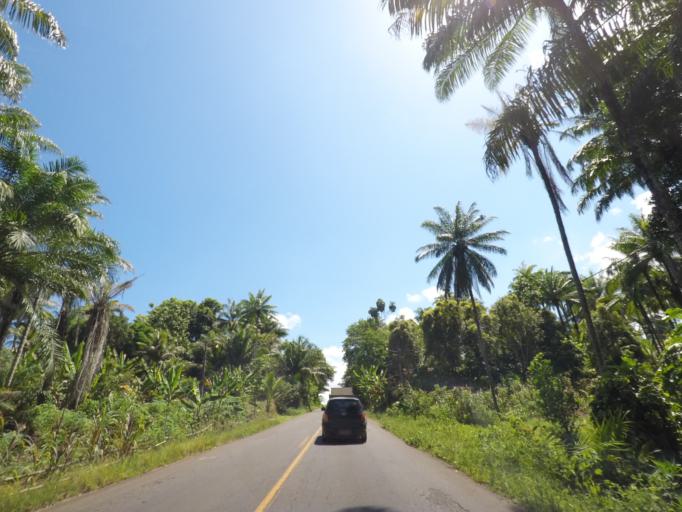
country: BR
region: Bahia
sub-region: Valenca
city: Valenca
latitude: -13.4513
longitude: -39.0863
